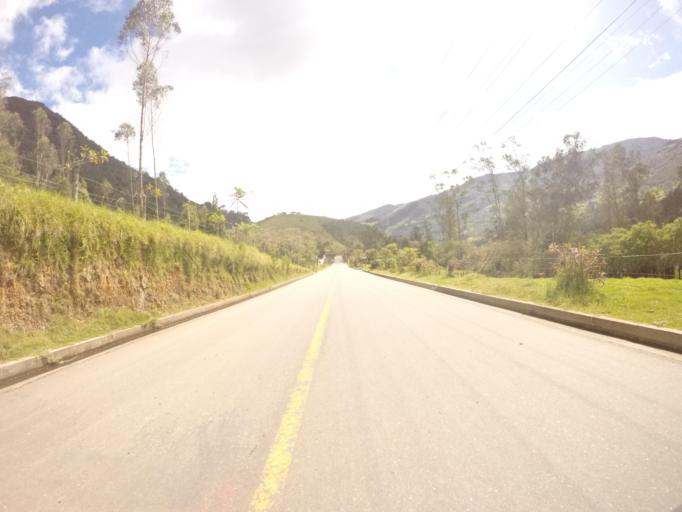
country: CO
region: Cauca
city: Jambalo
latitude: 2.7173
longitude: -76.3249
